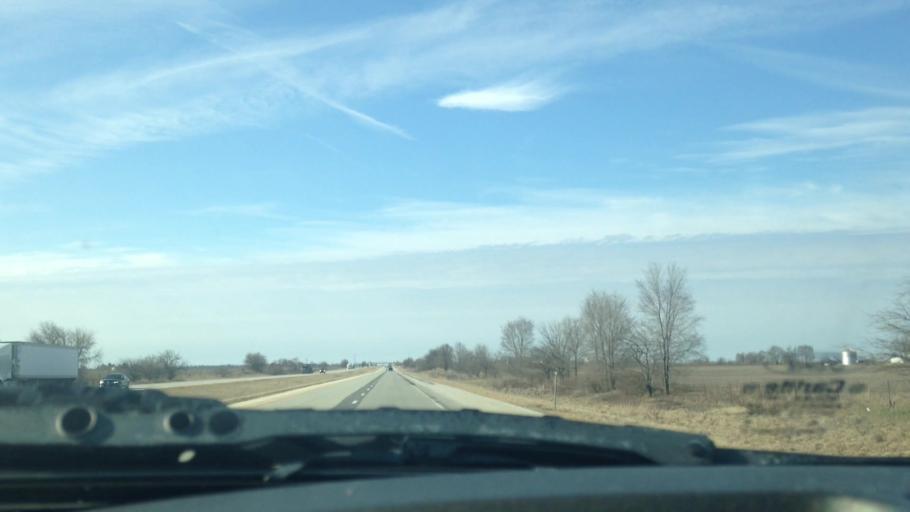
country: US
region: Illinois
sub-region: Ford County
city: Paxton
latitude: 40.5050
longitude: -88.0863
